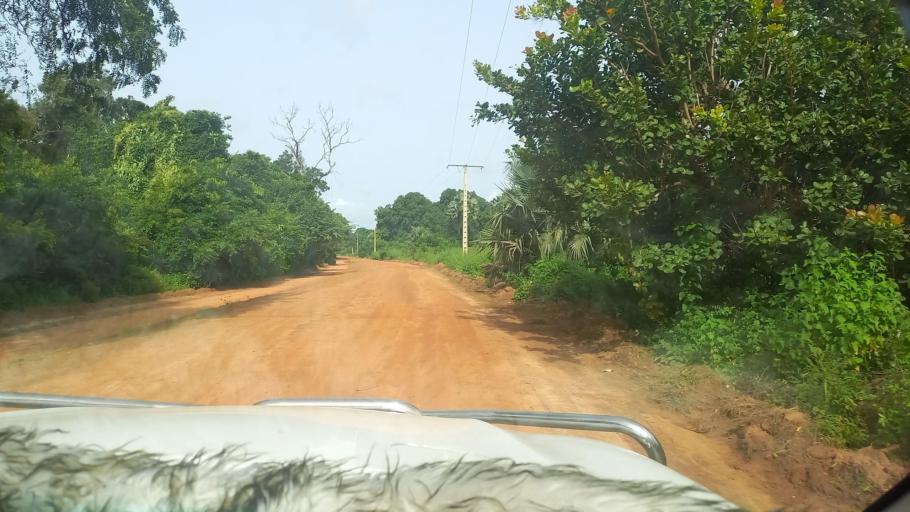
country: SN
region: Ziguinchor
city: Ziguinchor
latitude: 12.6696
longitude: -16.2706
